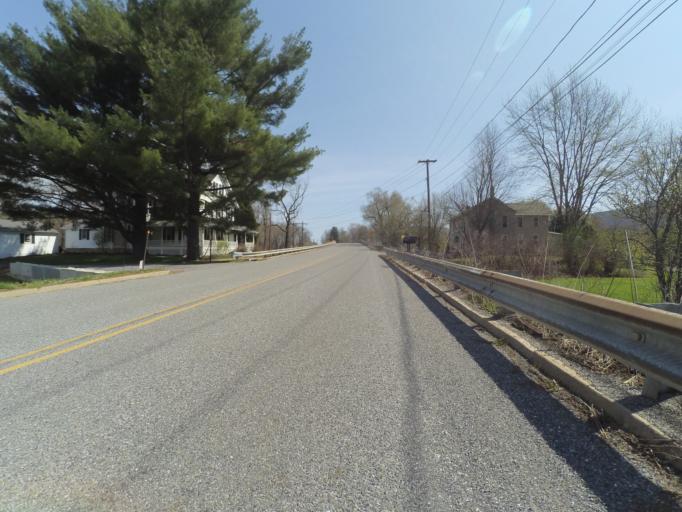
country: US
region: Pennsylvania
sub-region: Clinton County
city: Dunnstown
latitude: 41.1425
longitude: -77.3996
